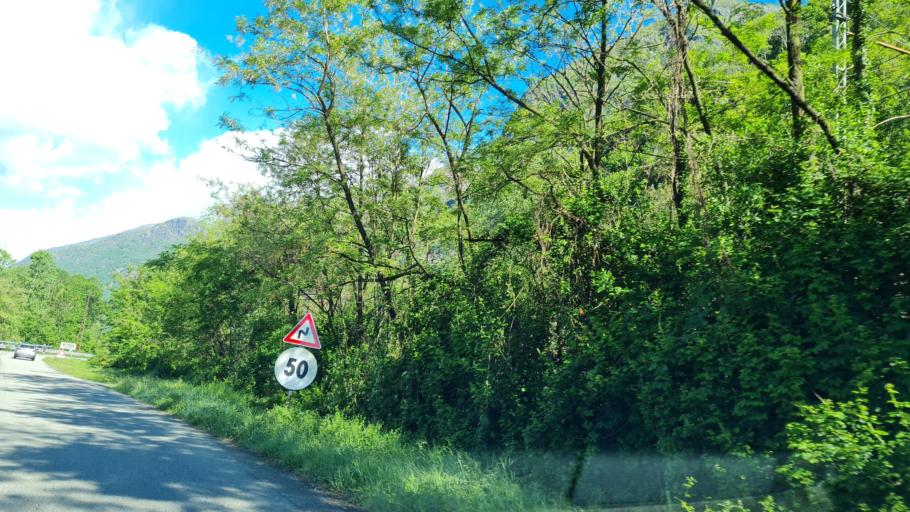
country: IT
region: Piedmont
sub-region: Provincia Verbano-Cusio-Ossola
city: Ornavasso
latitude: 45.9890
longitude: 8.4099
